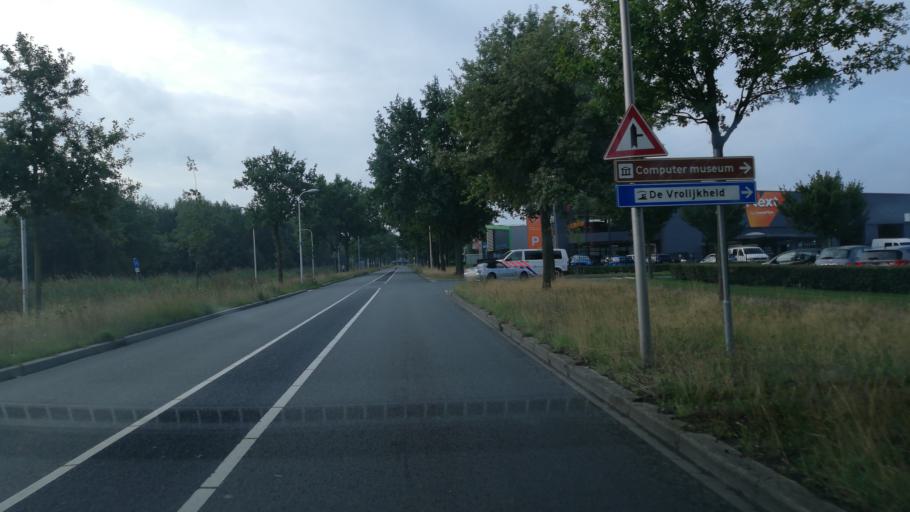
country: NL
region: Overijssel
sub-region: Gemeente Zwolle
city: Zwolle
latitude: 52.5251
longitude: 6.1240
